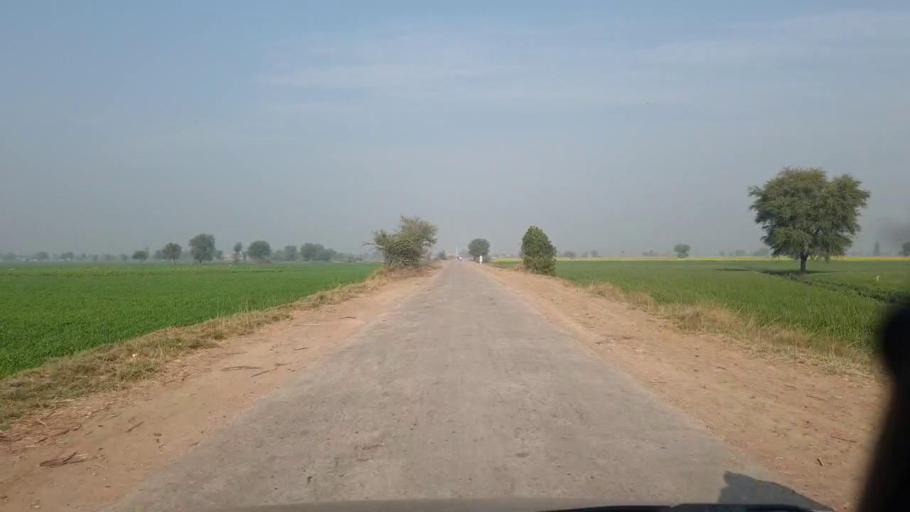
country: PK
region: Sindh
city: Shahdadpur
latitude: 25.9832
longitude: 68.5699
